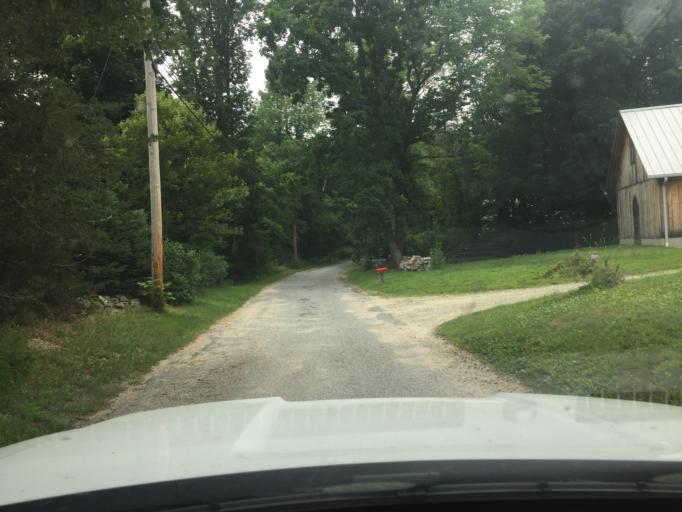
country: US
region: Connecticut
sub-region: New London County
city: Montville Center
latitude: 41.5722
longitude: -72.2072
